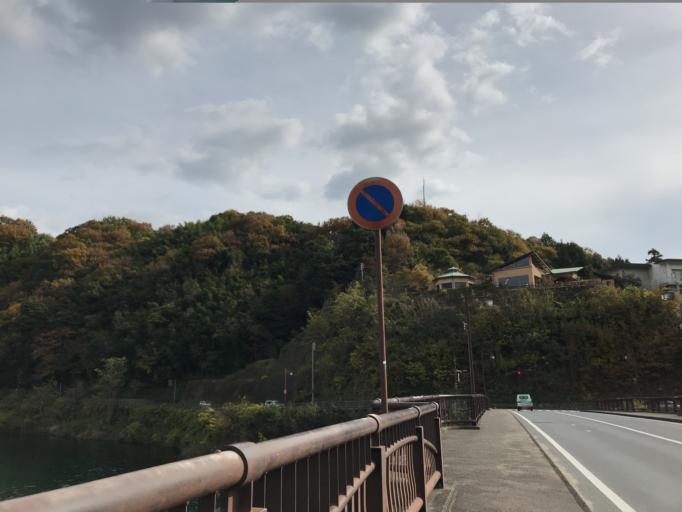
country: JP
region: Yamaguchi
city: Iwakuni
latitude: 34.1694
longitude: 132.1797
